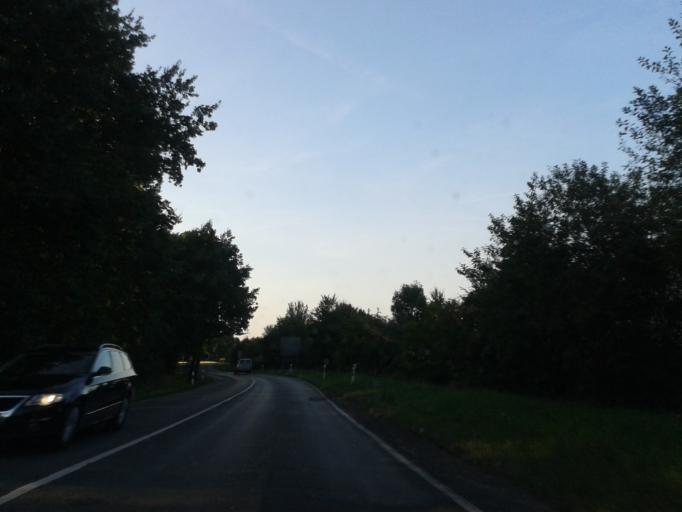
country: DE
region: Saxony
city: Klipphausen
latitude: 51.0674
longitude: 13.5184
